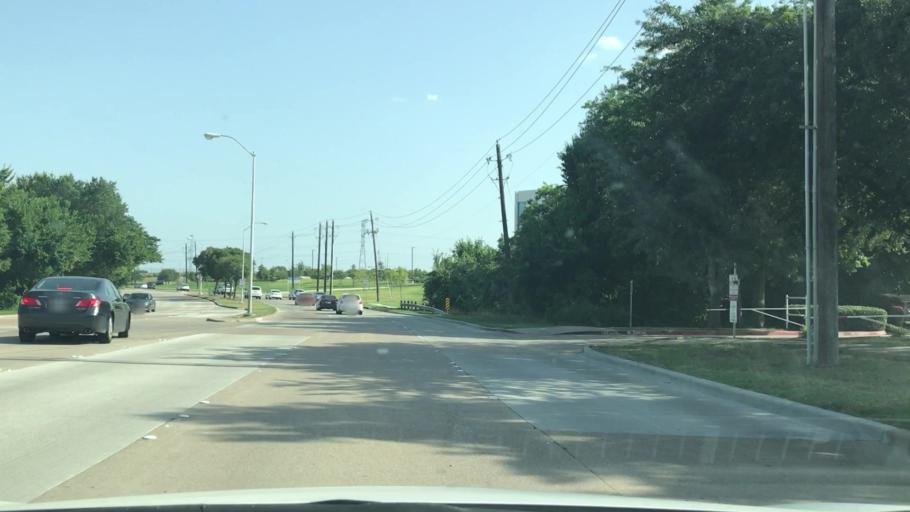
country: US
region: Texas
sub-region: Collin County
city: Plano
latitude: 33.0077
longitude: -96.7502
